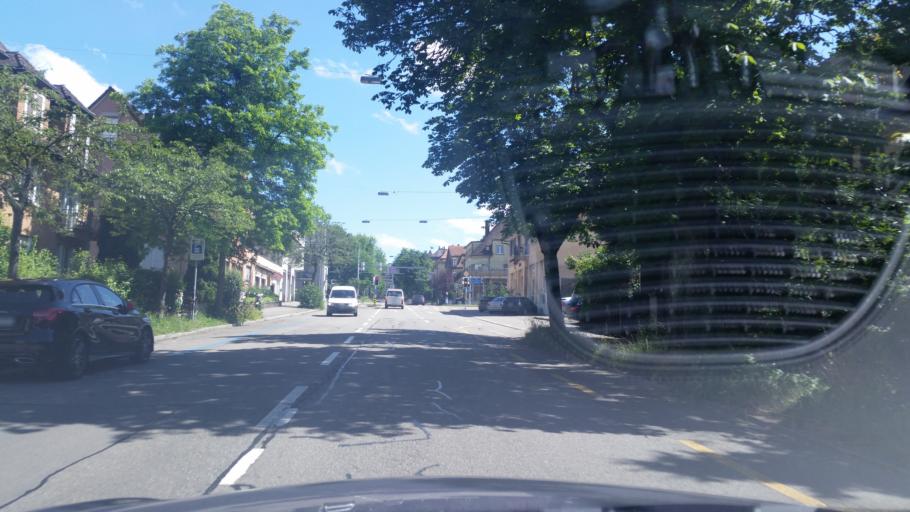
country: CH
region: Zurich
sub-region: Bezirk Zuerich
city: Zuerich (Kreis 6) / Unterstrass
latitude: 47.3994
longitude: 8.5384
